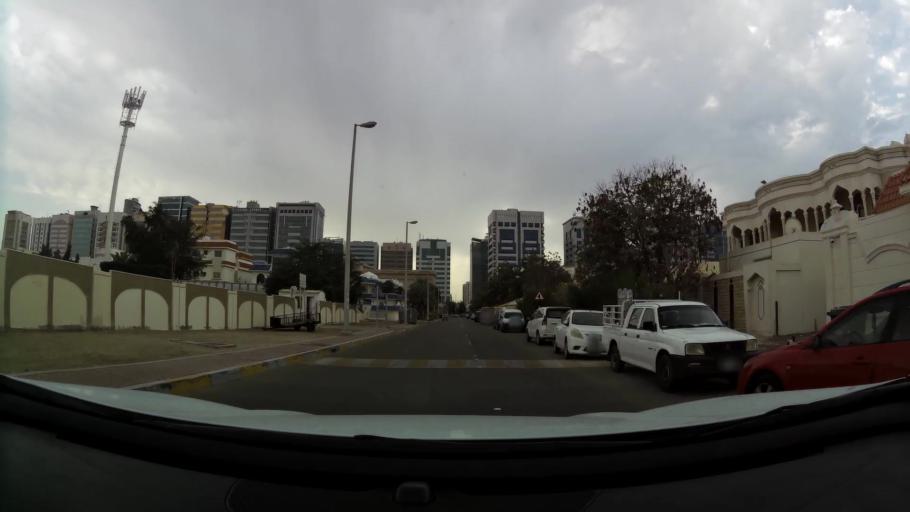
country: AE
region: Abu Dhabi
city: Abu Dhabi
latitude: 24.4780
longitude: 54.3751
